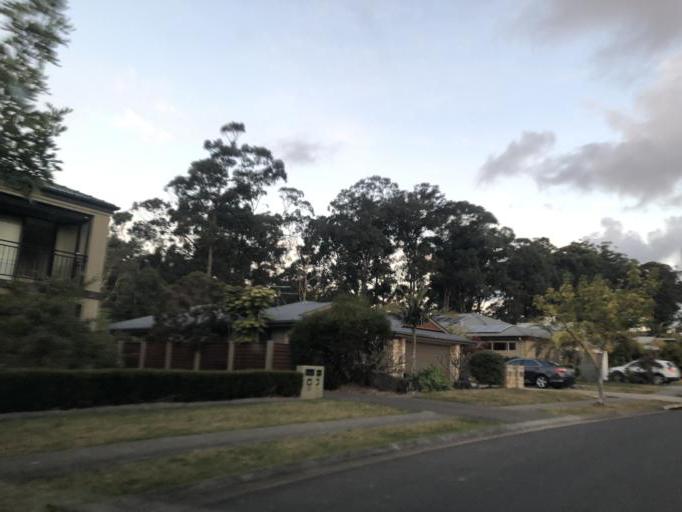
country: AU
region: New South Wales
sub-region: Coffs Harbour
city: Woolgoolga
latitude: -30.0939
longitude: 153.1926
